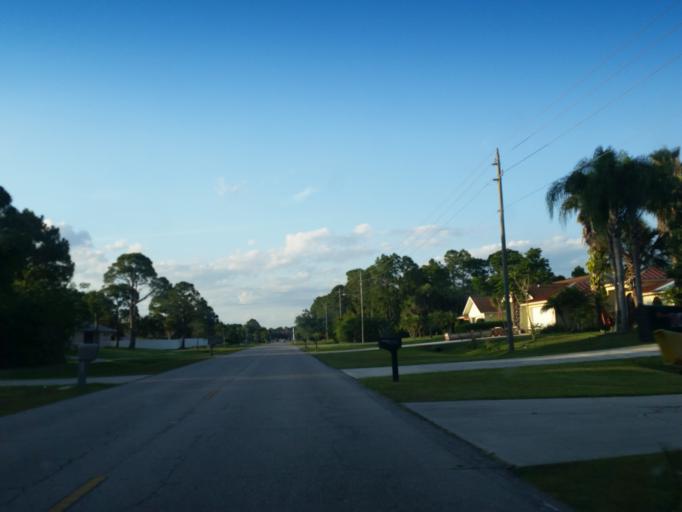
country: US
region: Florida
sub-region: Sarasota County
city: North Port
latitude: 27.0635
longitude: -82.1980
